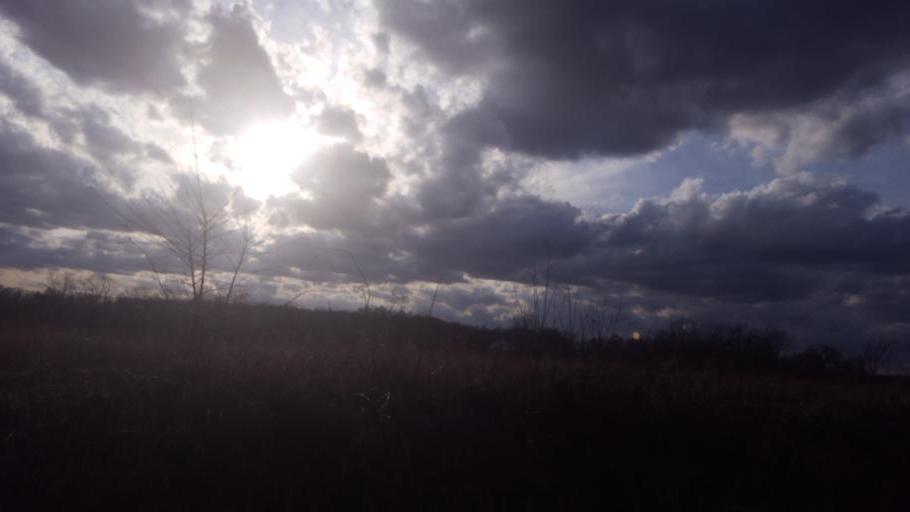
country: US
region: Ohio
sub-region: Knox County
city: Fredericktown
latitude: 40.4888
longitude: -82.4840
